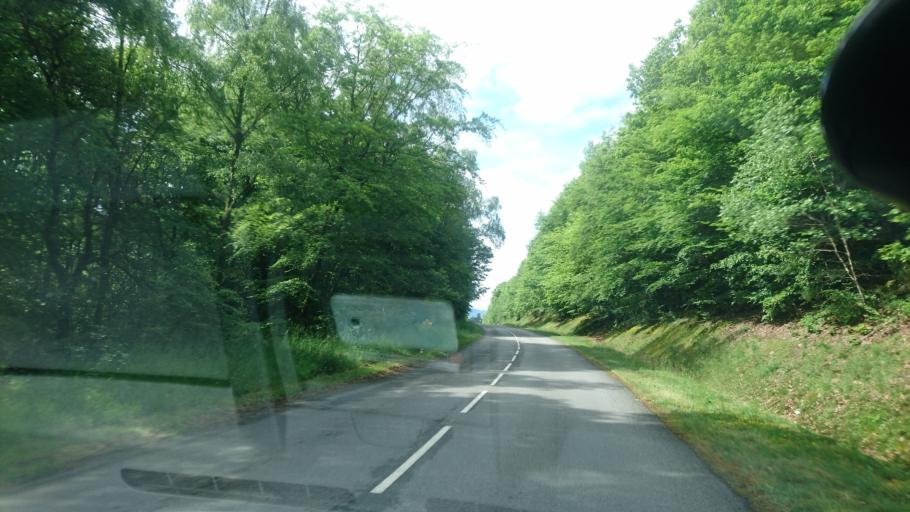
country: FR
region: Limousin
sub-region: Departement de la Haute-Vienne
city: Peyrat-le-Chateau
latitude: 45.7881
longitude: 1.8499
